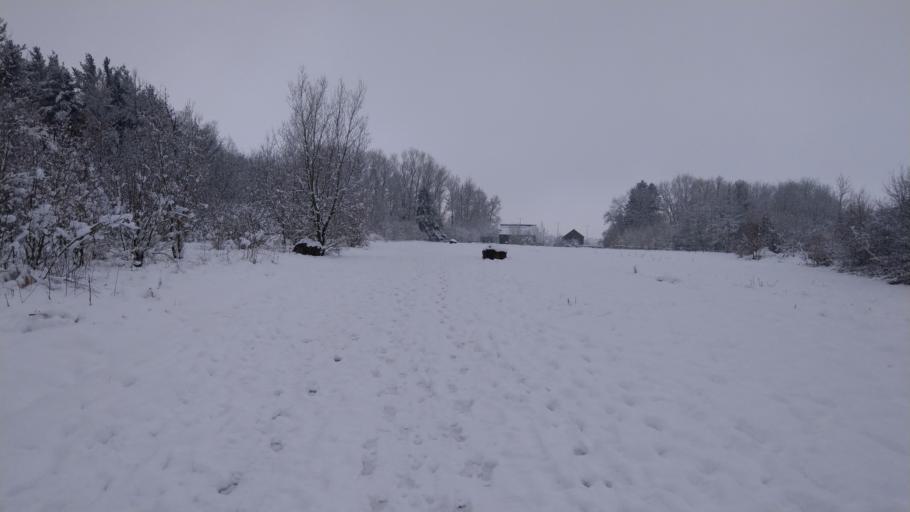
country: BE
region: Wallonia
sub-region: Province de Liege
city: Lontzen
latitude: 50.6858
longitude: 6.0510
